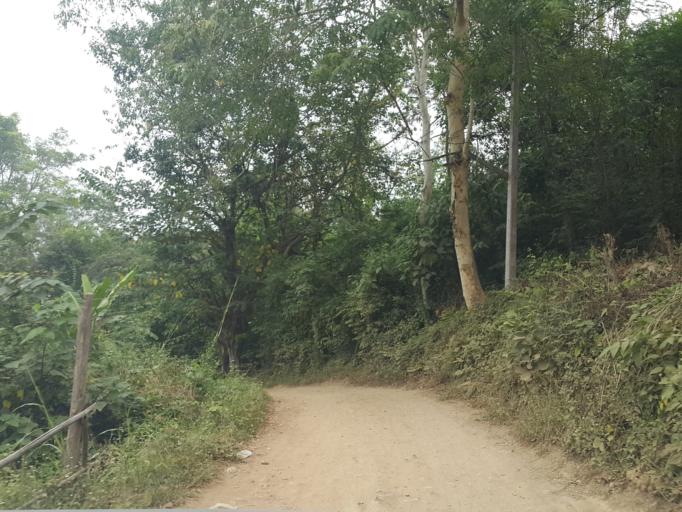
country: TH
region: Chiang Mai
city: Pai
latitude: 19.3599
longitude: 98.4483
